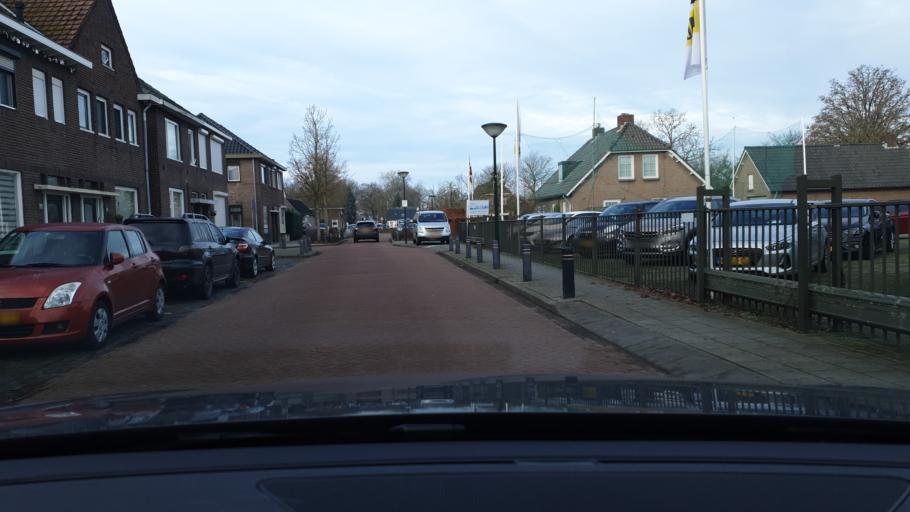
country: NL
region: North Brabant
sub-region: Gemeente Geldrop-Mierlo
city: Geldrop
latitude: 51.4298
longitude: 5.5445
